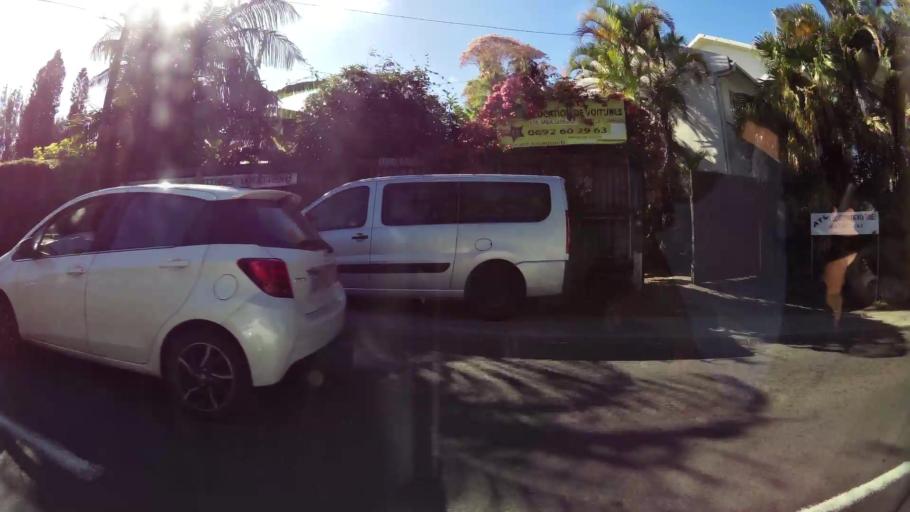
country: RE
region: Reunion
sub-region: Reunion
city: Le Tampon
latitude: -21.2821
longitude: 55.5243
